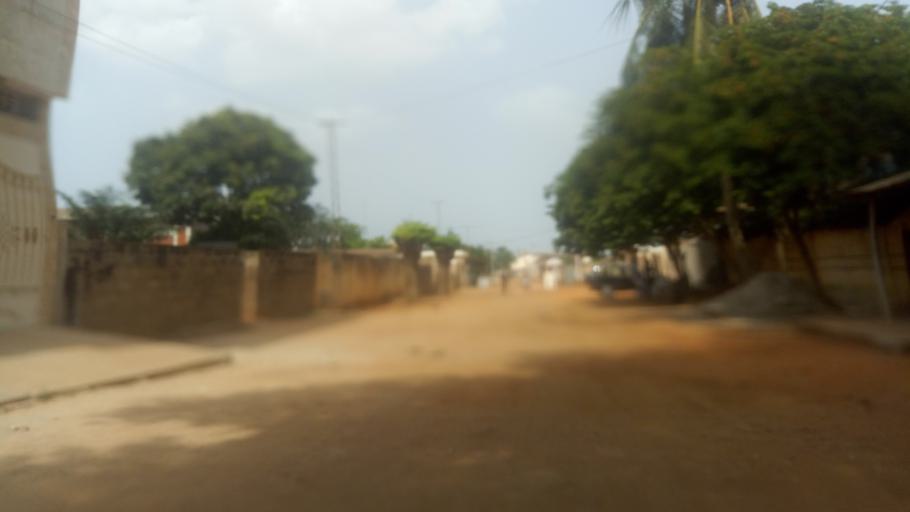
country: TG
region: Maritime
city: Lome
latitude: 6.1762
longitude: 1.1896
